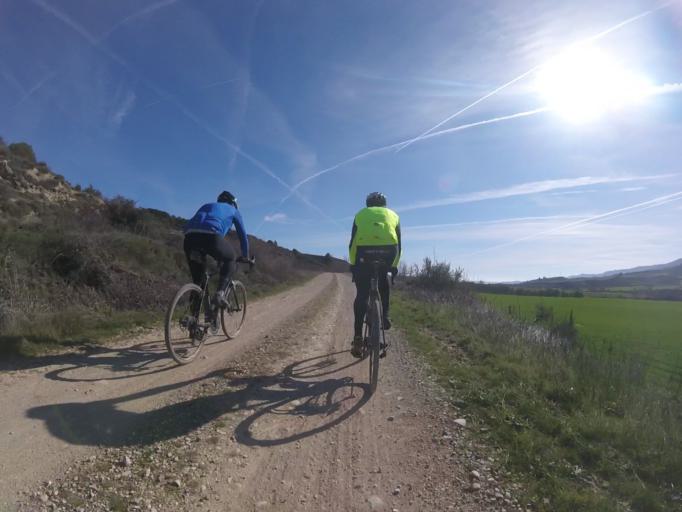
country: ES
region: Navarre
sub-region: Provincia de Navarra
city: Cirauqui
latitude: 42.6655
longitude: -1.8999
